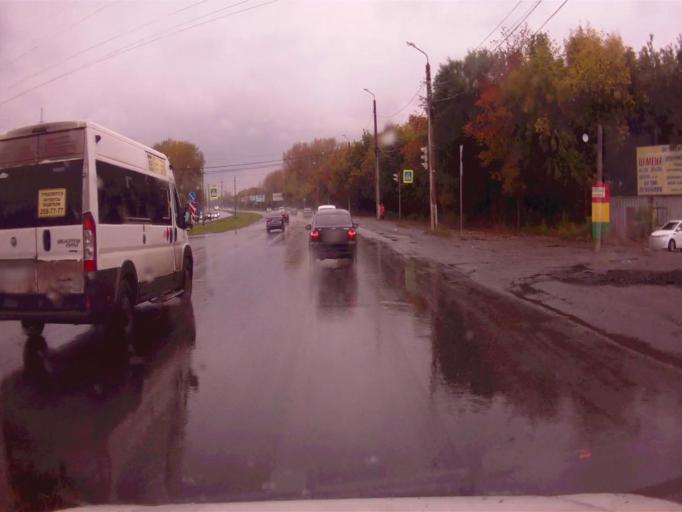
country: RU
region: Chelyabinsk
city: Dolgoderevenskoye
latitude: 55.2412
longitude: 61.3611
